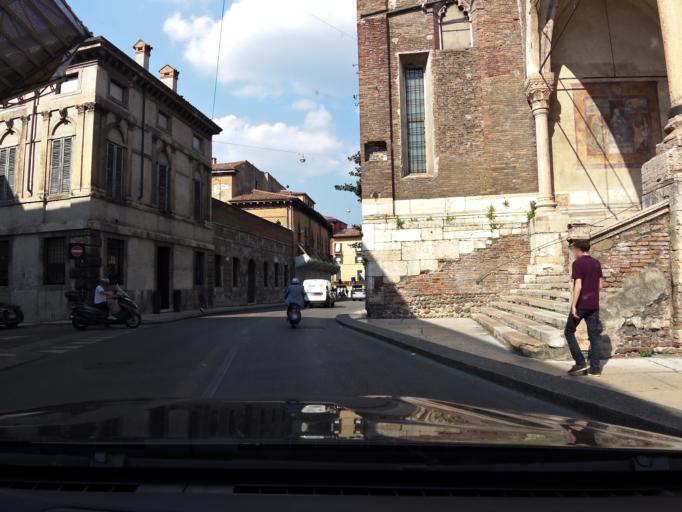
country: IT
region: Veneto
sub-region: Provincia di Verona
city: Verona
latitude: 45.4392
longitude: 10.9994
